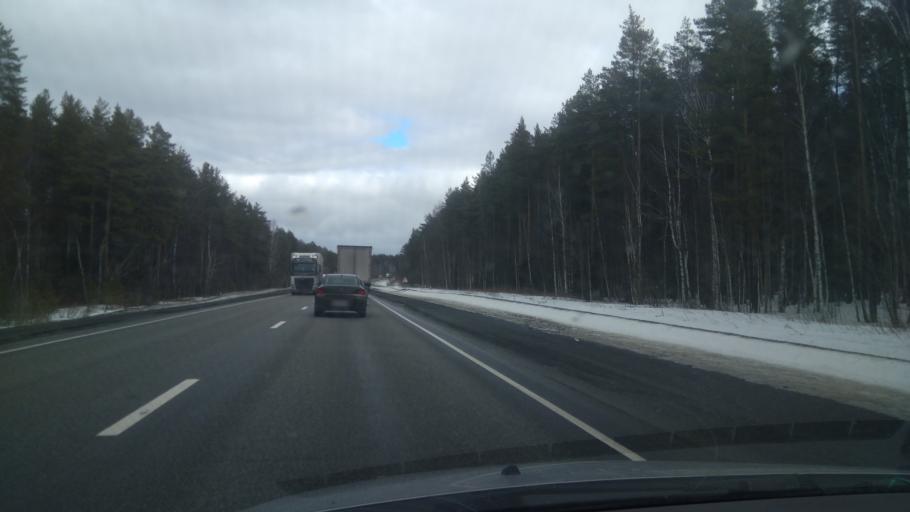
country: RU
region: Sverdlovsk
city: Bisert'
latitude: 56.8269
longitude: 58.7707
